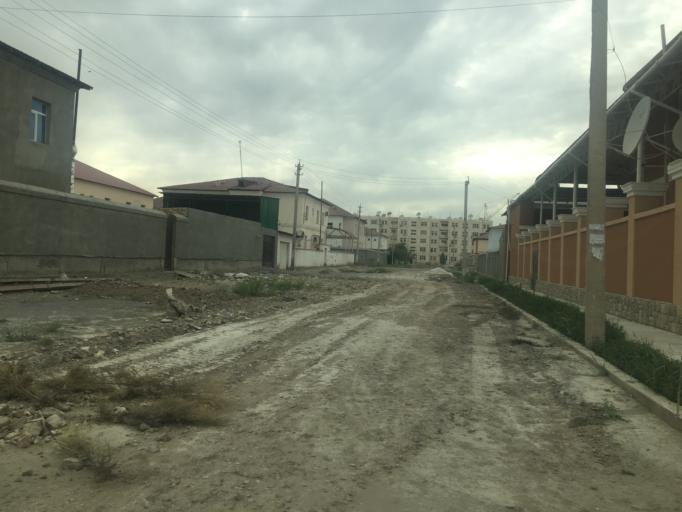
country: TM
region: Dasoguz
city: Dasoguz
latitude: 41.8377
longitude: 59.9338
